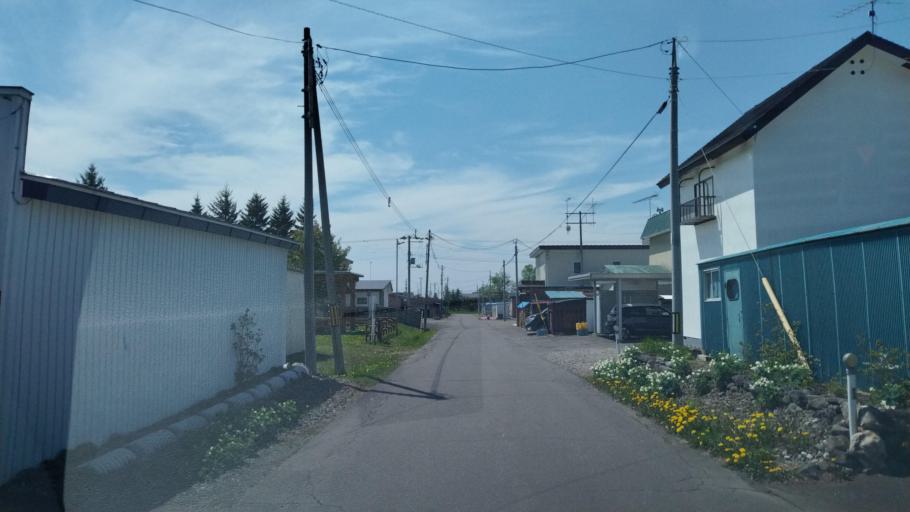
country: JP
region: Hokkaido
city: Otofuke
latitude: 43.2403
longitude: 143.2913
